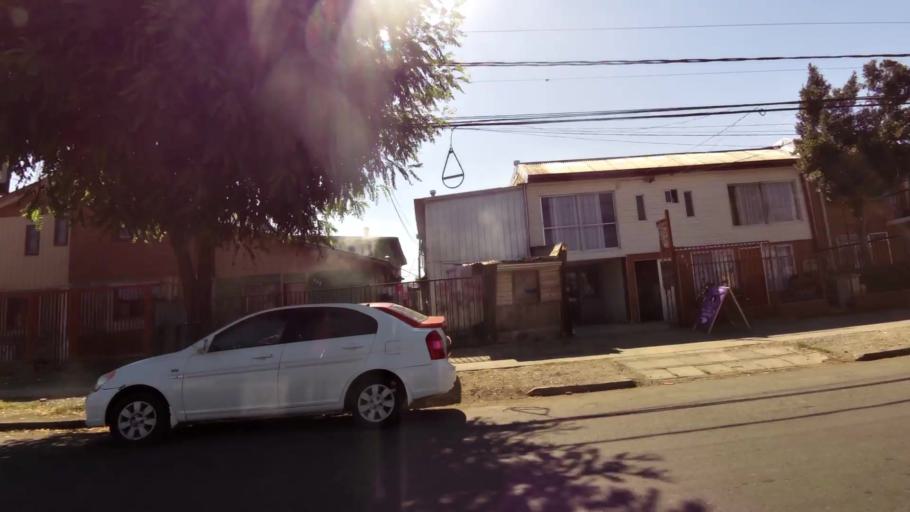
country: CL
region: Biobio
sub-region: Provincia de Concepcion
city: Concepcion
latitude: -36.7957
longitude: -73.0363
